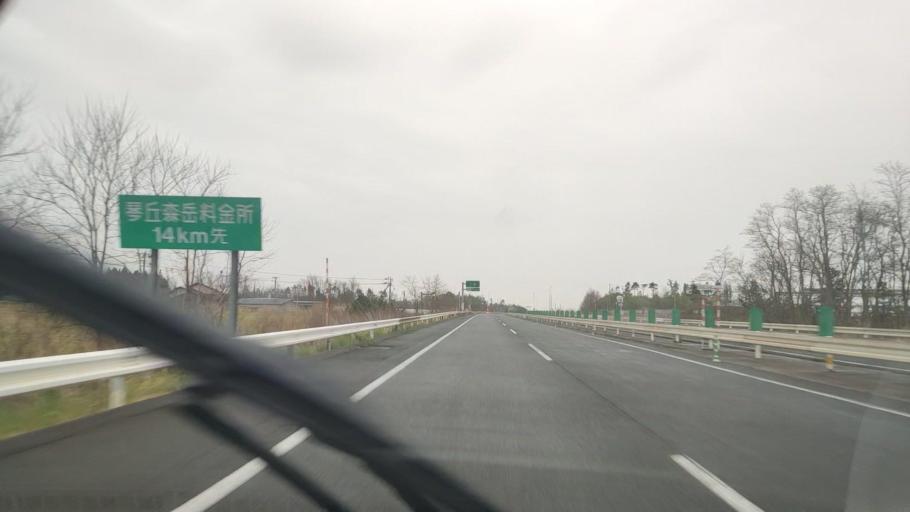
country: JP
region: Akita
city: Noshiromachi
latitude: 40.1236
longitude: 140.0122
